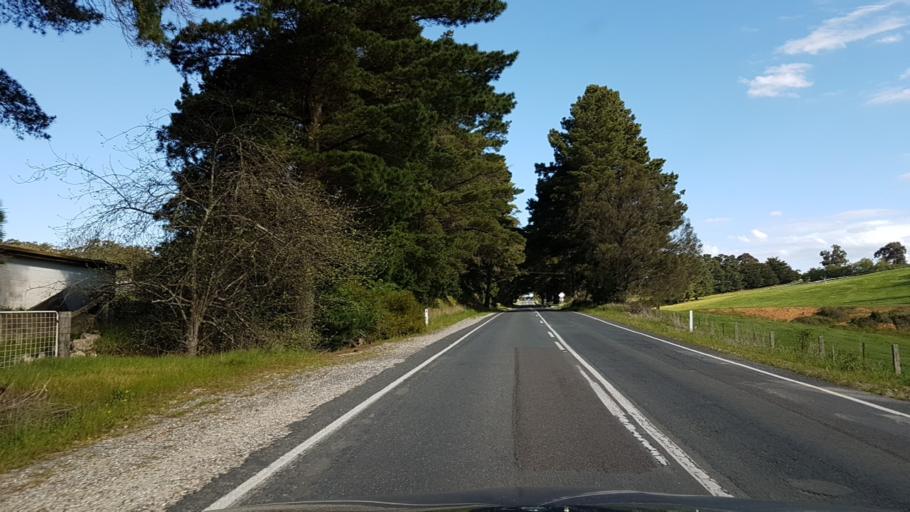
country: AU
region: South Australia
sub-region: Adelaide Hills
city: Lobethal
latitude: -34.8730
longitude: 138.8894
